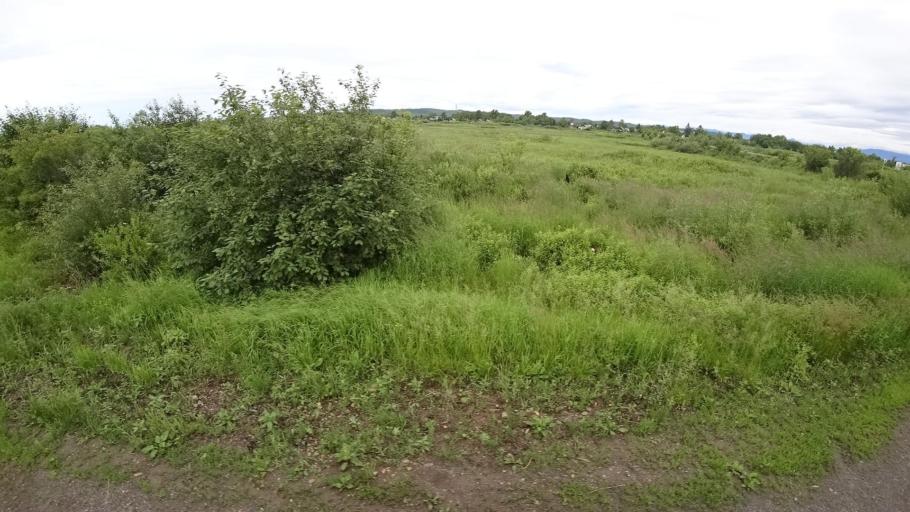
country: RU
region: Khabarovsk Krai
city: Amursk
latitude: 49.8959
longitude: 136.1465
